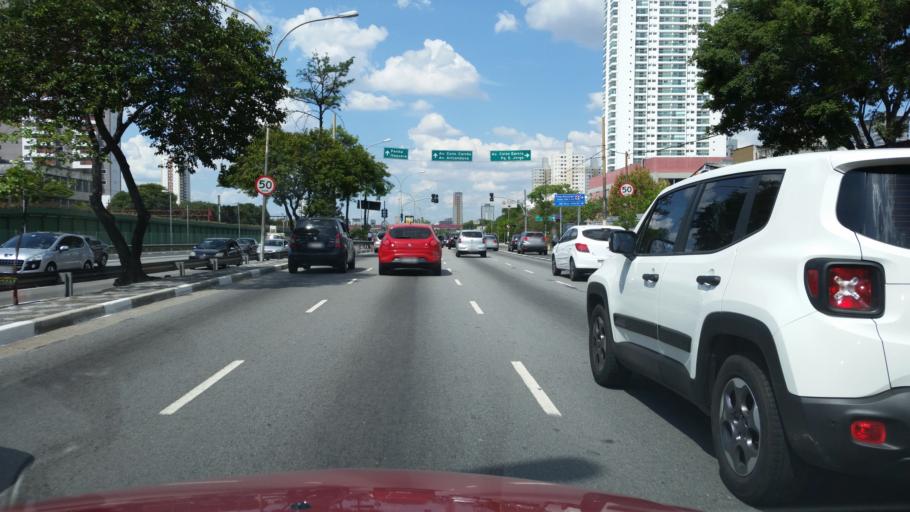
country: BR
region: Sao Paulo
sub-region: Sao Paulo
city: Sao Paulo
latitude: -23.5395
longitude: -46.5713
